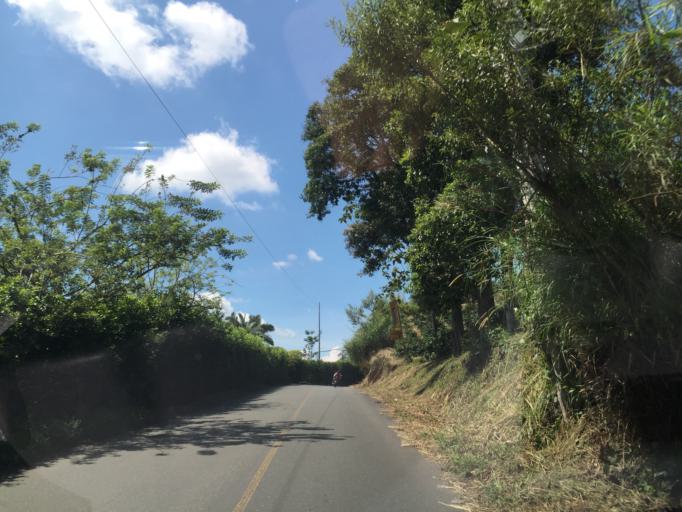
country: CO
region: Valle del Cauca
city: Alcala
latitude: 4.7012
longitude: -75.7916
